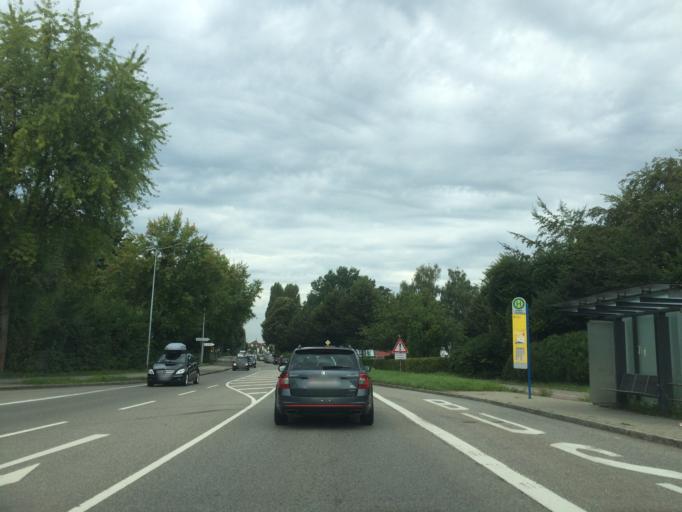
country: DE
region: Baden-Wuerttemberg
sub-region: Tuebingen Region
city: Immenstaad am Bodensee
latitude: 47.6685
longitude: 9.4212
